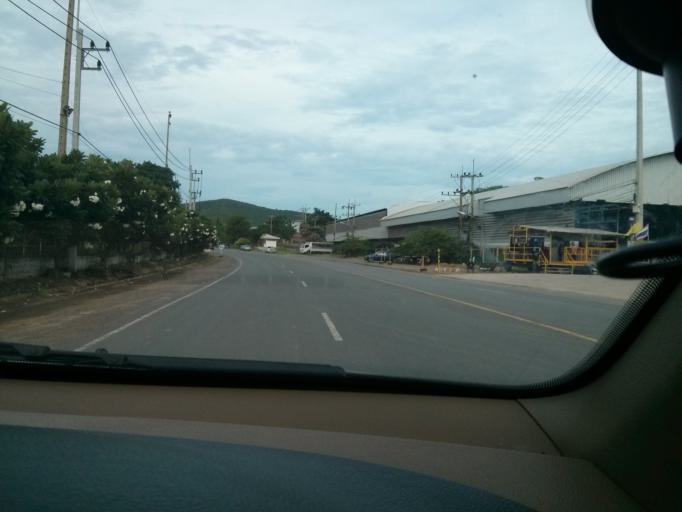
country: TH
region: Chon Buri
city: Sattahip
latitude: 12.6244
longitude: 100.9195
